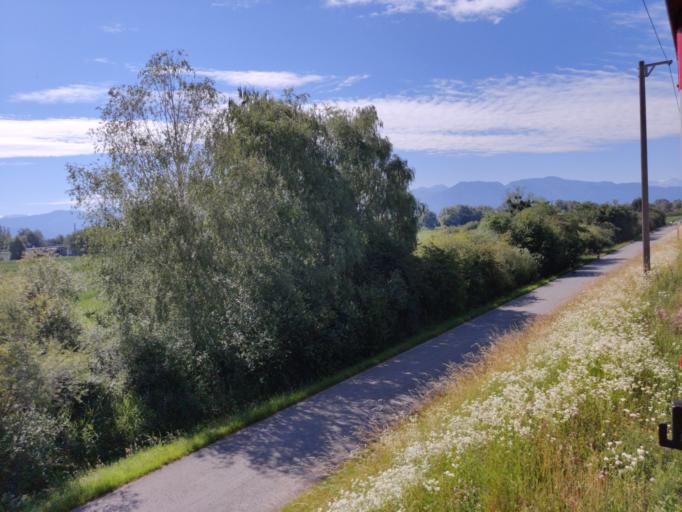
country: AT
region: Vorarlberg
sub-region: Politischer Bezirk Bregenz
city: Fussach
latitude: 47.4851
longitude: 9.6716
